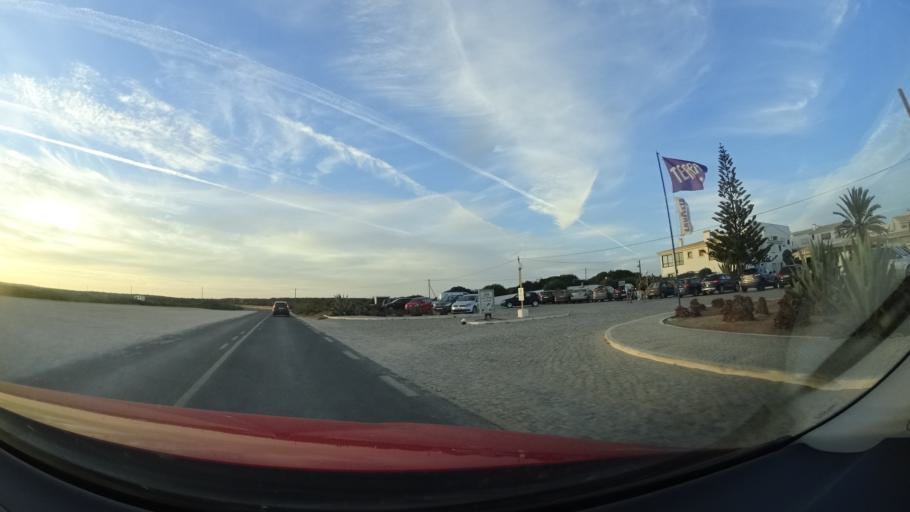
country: PT
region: Faro
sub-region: Vila do Bispo
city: Sagres
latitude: 37.0266
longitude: -8.9633
